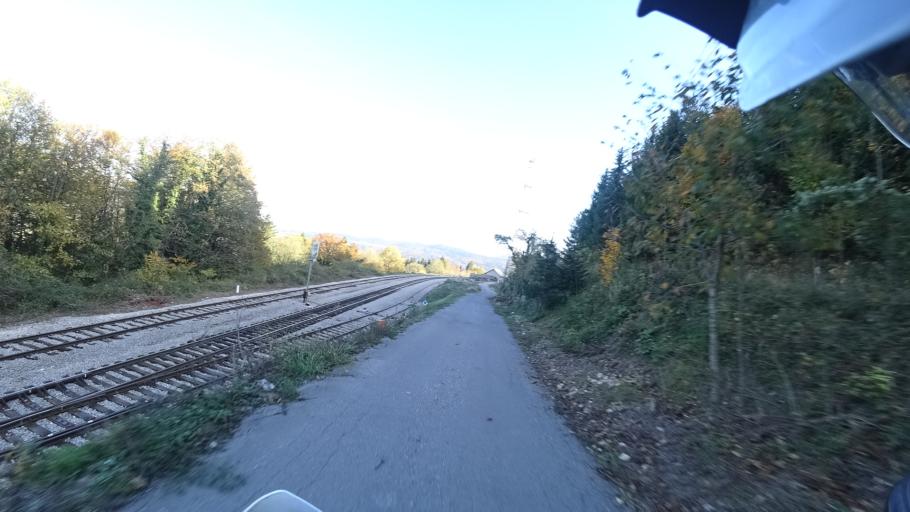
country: HR
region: Karlovacka
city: Plaski
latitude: 44.9792
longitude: 15.4271
